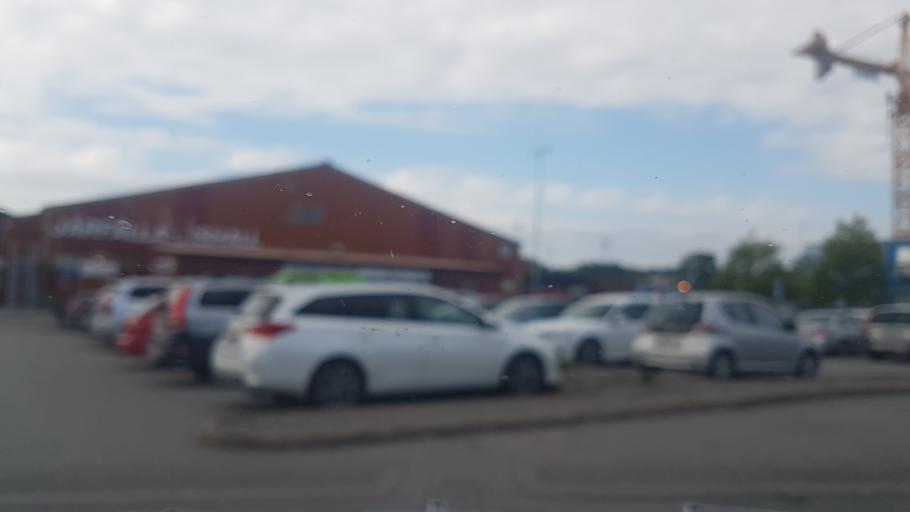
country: SE
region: Stockholm
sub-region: Jarfalla Kommun
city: Jakobsberg
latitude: 59.4181
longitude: 17.8252
